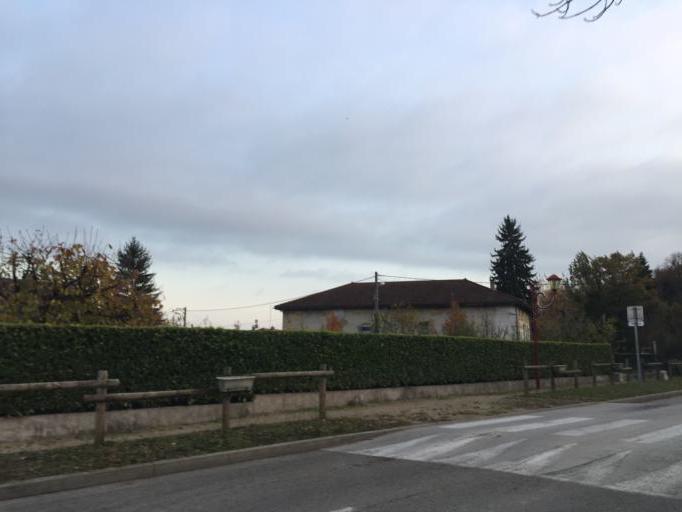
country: FR
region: Rhone-Alpes
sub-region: Departement de l'Ain
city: Chatillon-la-Palud
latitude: 45.9430
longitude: 5.2432
